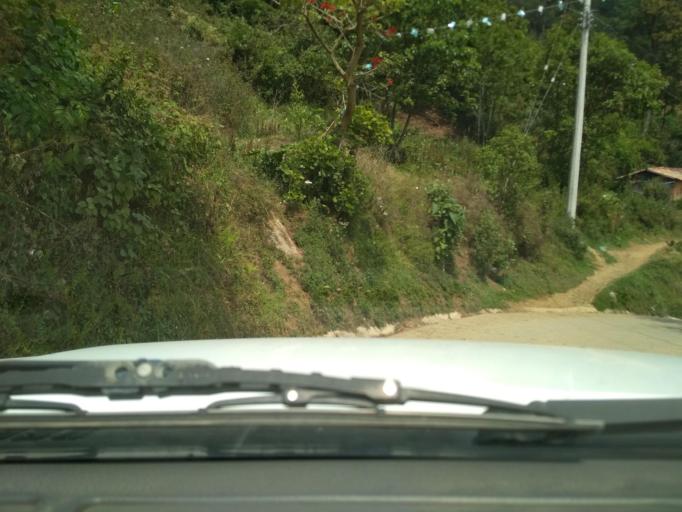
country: MX
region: Veracruz
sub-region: Camerino Z. Mendoza
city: Necoxtla
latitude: 18.7765
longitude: -97.1563
